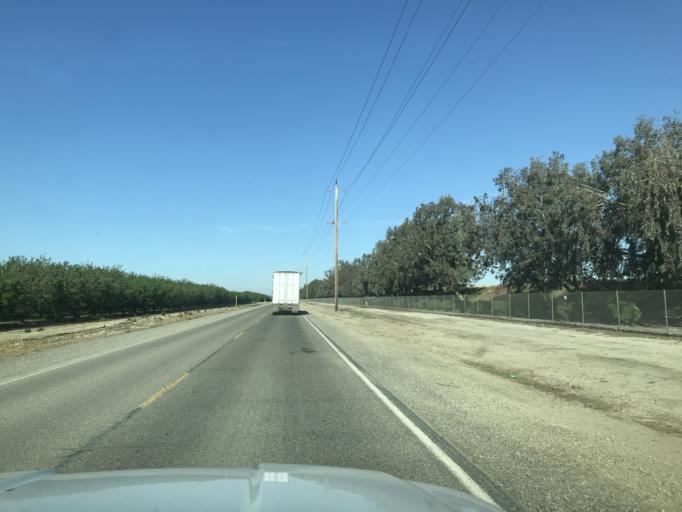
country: US
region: California
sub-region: Fresno County
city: San Joaquin
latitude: 36.6618
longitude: -120.1250
